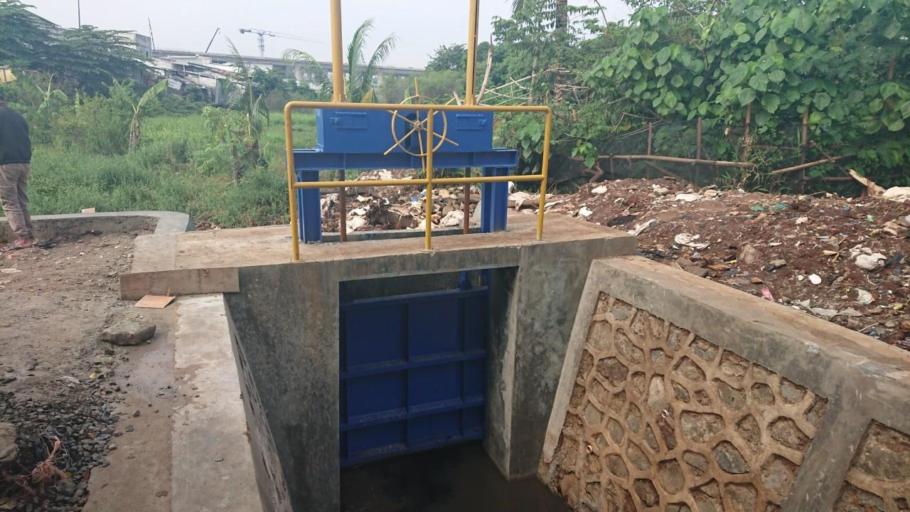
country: ID
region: Jakarta Raya
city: Jakarta
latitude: -6.2412
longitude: 106.8877
